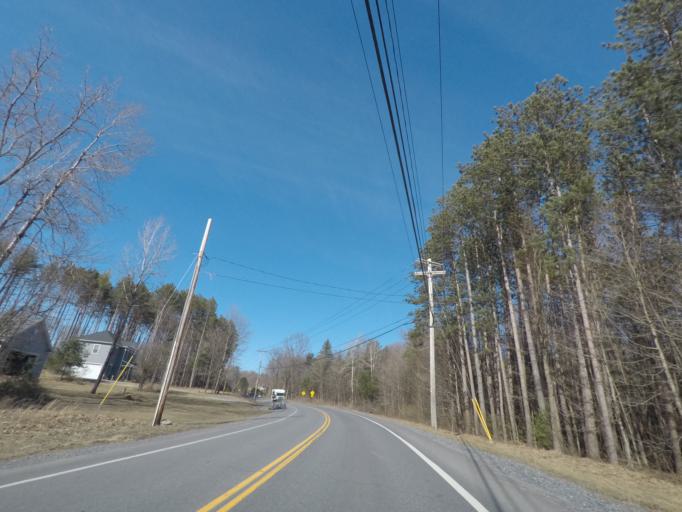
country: US
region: New York
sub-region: Saratoga County
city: Milton
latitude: 43.0682
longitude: -73.8484
